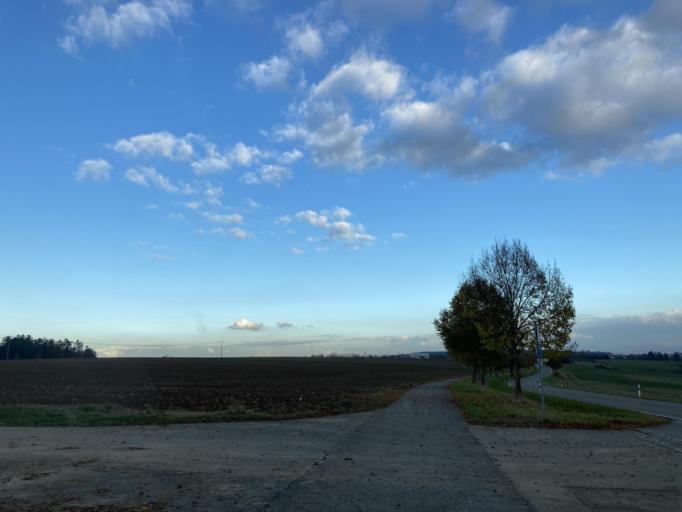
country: DE
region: Baden-Wuerttemberg
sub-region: Tuebingen Region
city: Haigerloch
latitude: 48.4323
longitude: 8.7941
